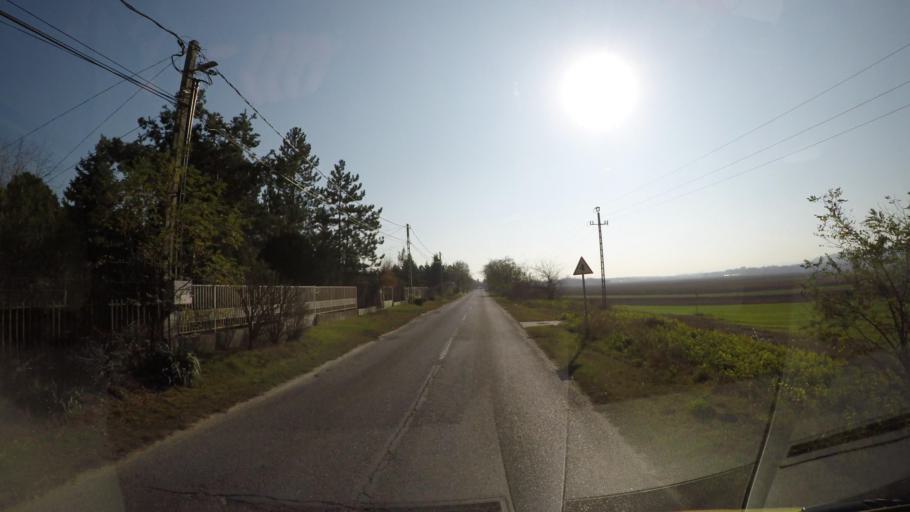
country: HU
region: Pest
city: Leanyfalu
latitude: 47.7099
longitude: 19.1066
